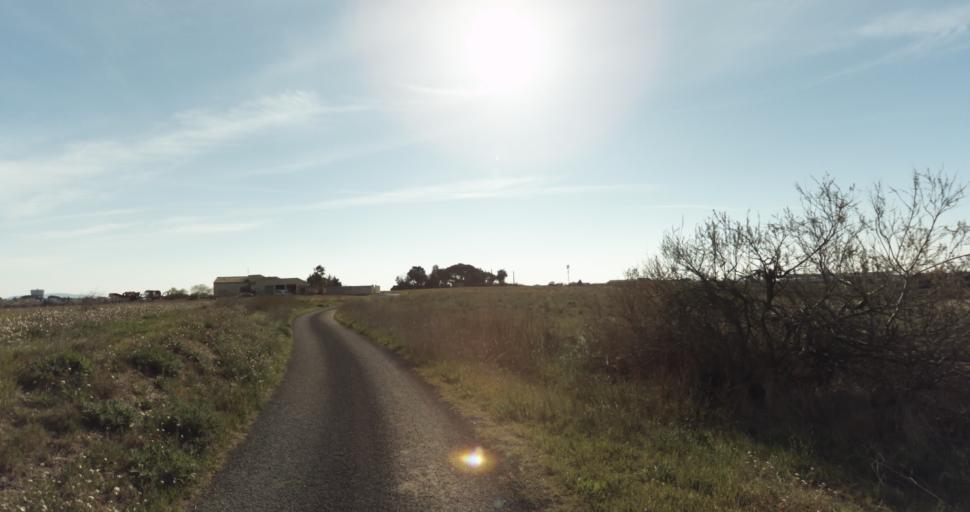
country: FR
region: Languedoc-Roussillon
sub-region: Departement de l'Herault
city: Marseillan
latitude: 43.3602
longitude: 3.5131
